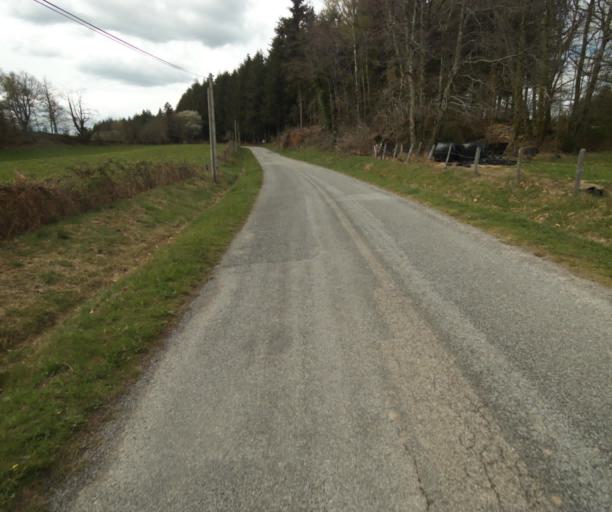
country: FR
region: Limousin
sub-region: Departement de la Correze
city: Argentat
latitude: 45.1881
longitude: 1.9344
